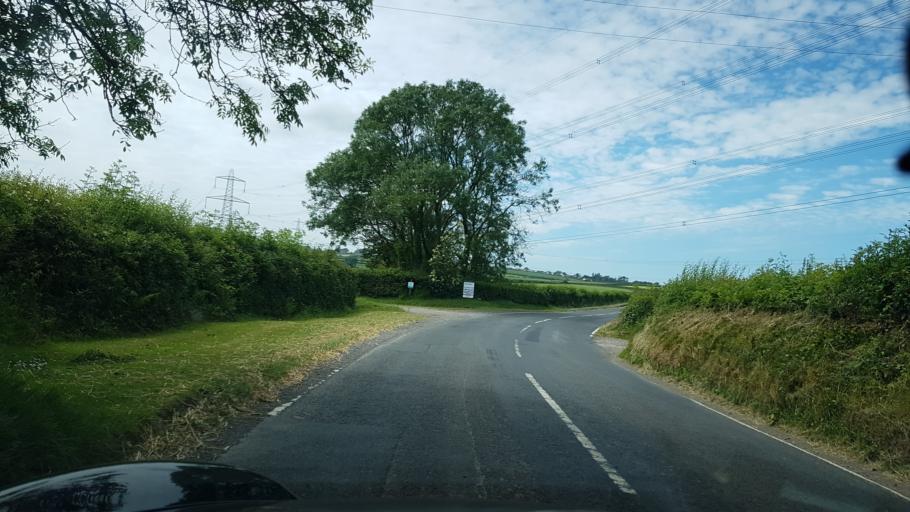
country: GB
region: Wales
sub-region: Carmarthenshire
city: Whitland
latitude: 51.7788
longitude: -4.6202
